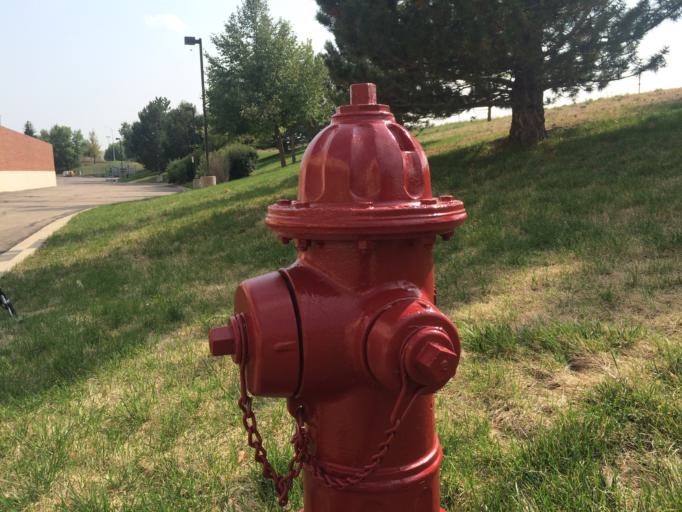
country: US
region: Colorado
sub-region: Boulder County
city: Superior
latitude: 39.9612
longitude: -105.1702
